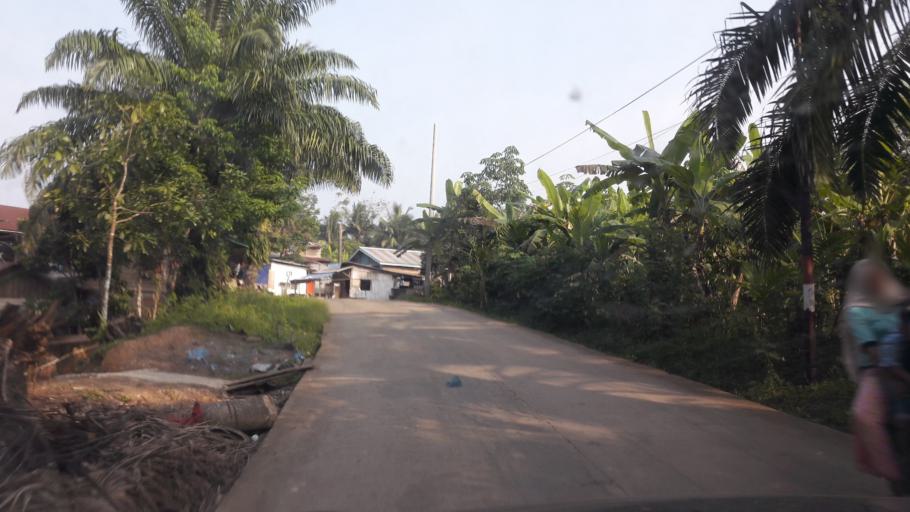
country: ID
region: South Sumatra
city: Gunungmegang Dalam
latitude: -3.2656
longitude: 103.8179
